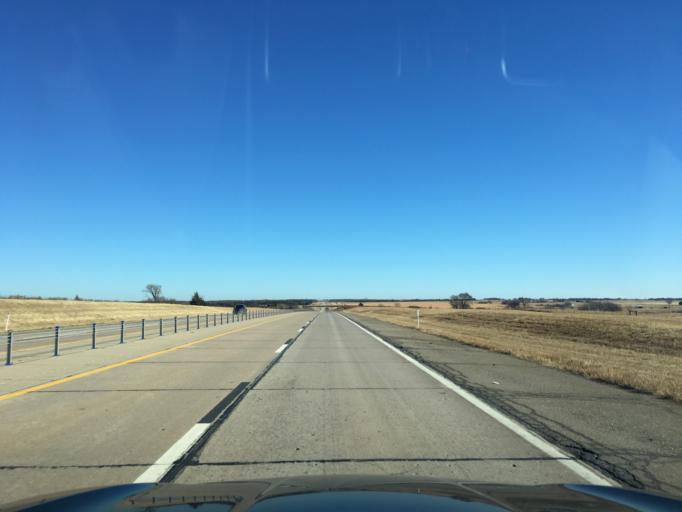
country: US
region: Oklahoma
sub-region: Pawnee County
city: Pawnee
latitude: 36.2252
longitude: -96.8631
